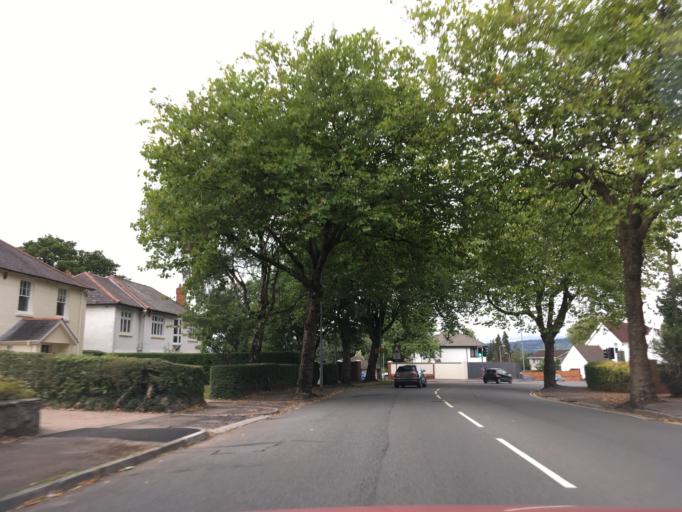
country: GB
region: Wales
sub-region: Cardiff
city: Cardiff
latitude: 51.5073
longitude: -3.1649
